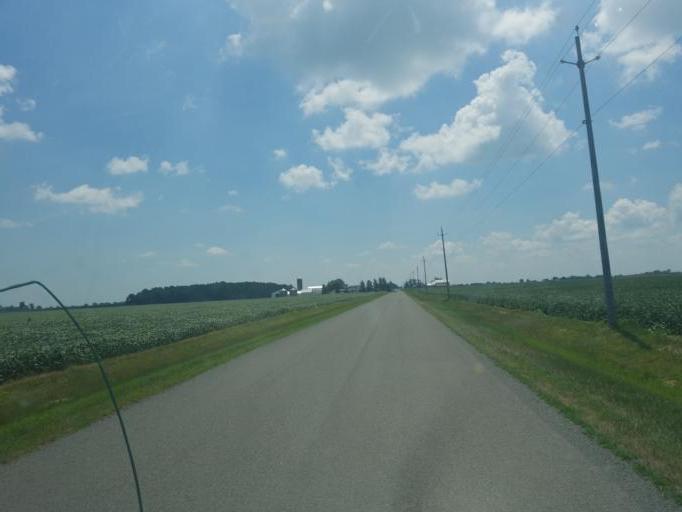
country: US
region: Ohio
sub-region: Mercer County
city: Celina
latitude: 40.5674
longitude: -84.4940
